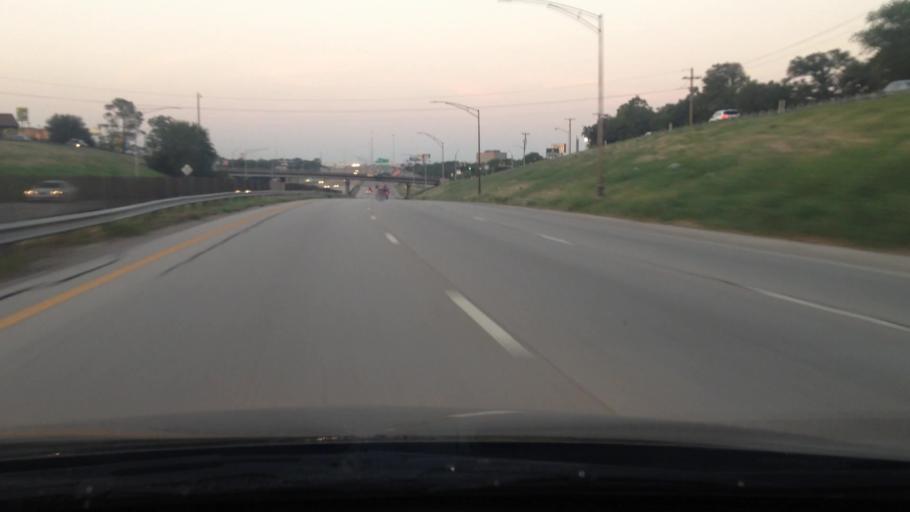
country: US
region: Texas
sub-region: Tarrant County
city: Haltom City
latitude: 32.7437
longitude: -97.2237
